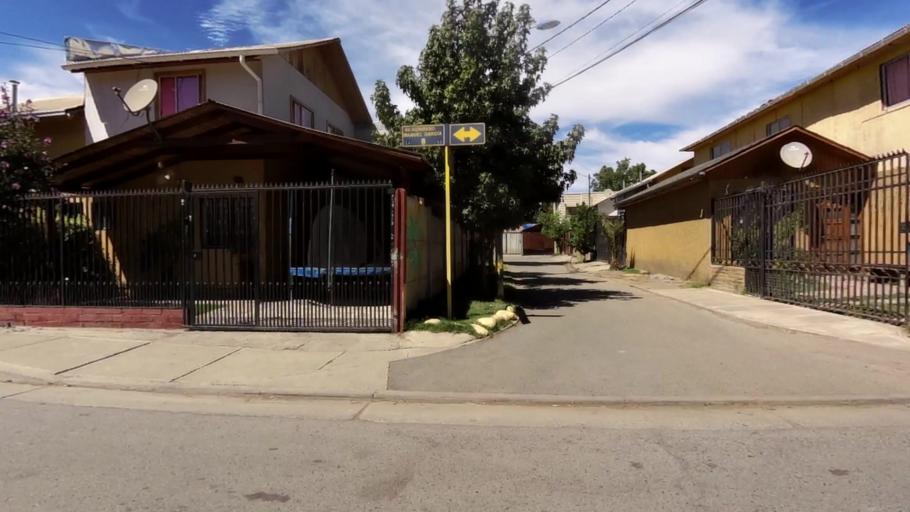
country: CL
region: O'Higgins
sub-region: Provincia de Cachapoal
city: Graneros
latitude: -33.9830
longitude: -70.7151
